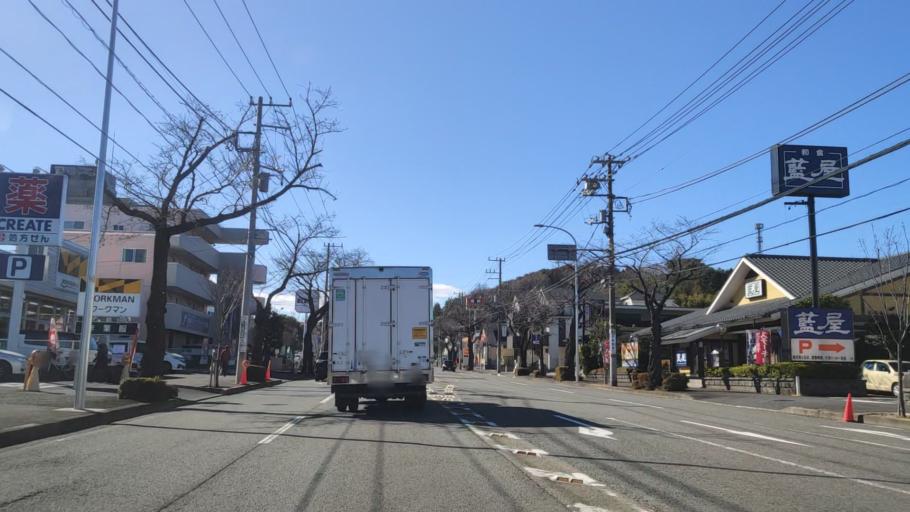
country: JP
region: Tokyo
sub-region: Machida-shi
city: Machida
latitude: 35.5178
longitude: 139.5030
